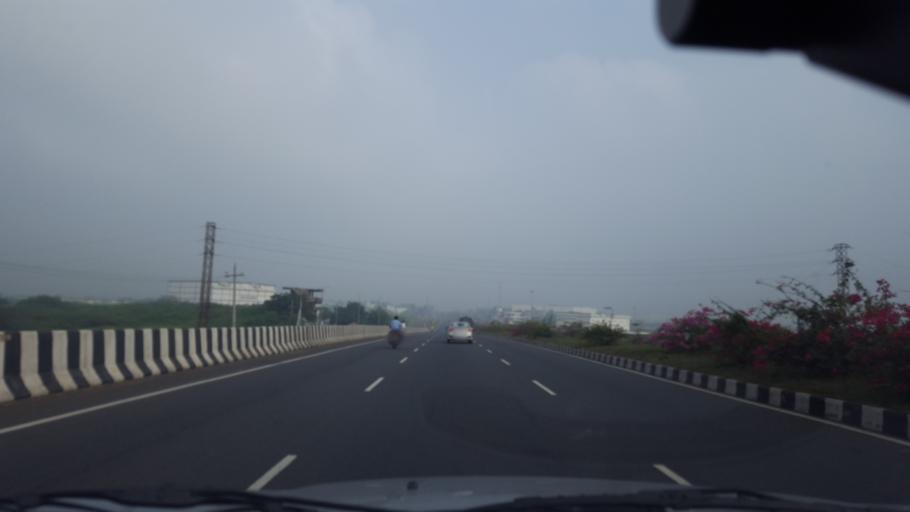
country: IN
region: Andhra Pradesh
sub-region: Prakasam
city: Ongole
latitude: 15.5535
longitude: 80.0553
